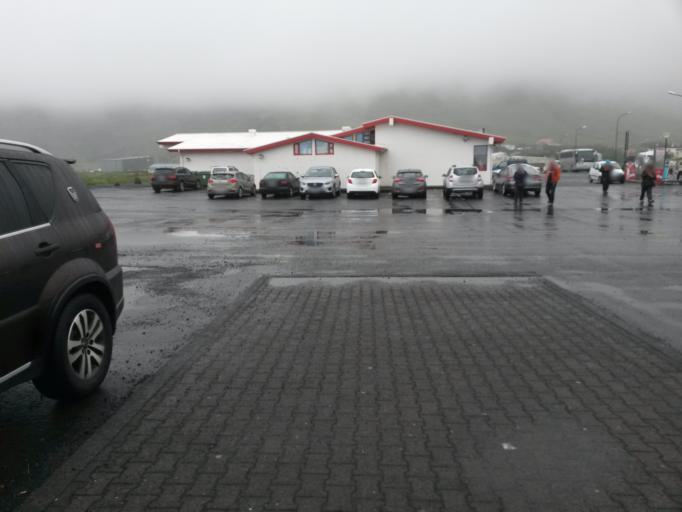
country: IS
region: South
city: Vestmannaeyjar
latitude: 63.4176
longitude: -19.0002
